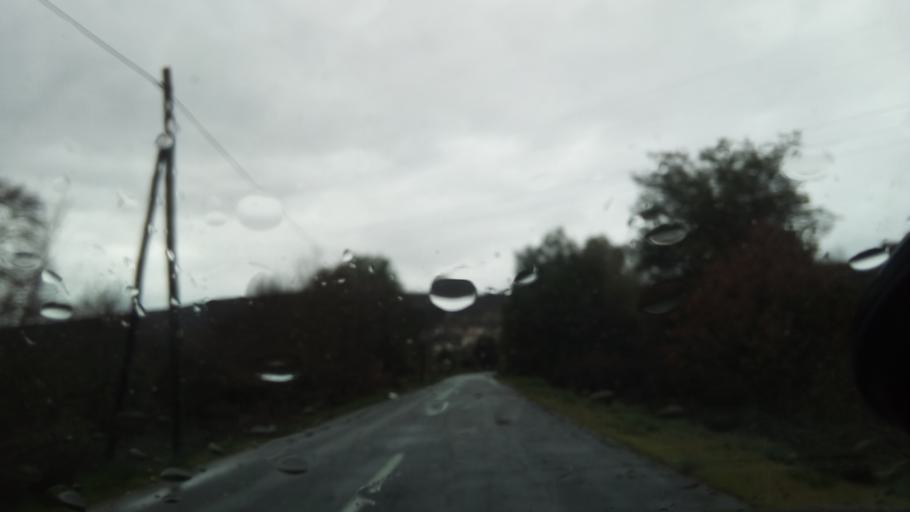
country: PT
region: Guarda
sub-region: Celorico da Beira
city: Celorico da Beira
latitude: 40.6254
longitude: -7.4294
